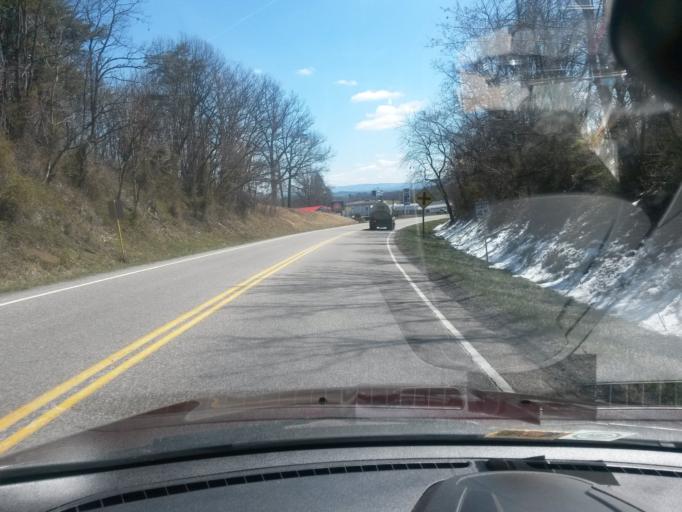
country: US
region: Virginia
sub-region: Augusta County
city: Jolivue
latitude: 38.0787
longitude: -79.0915
